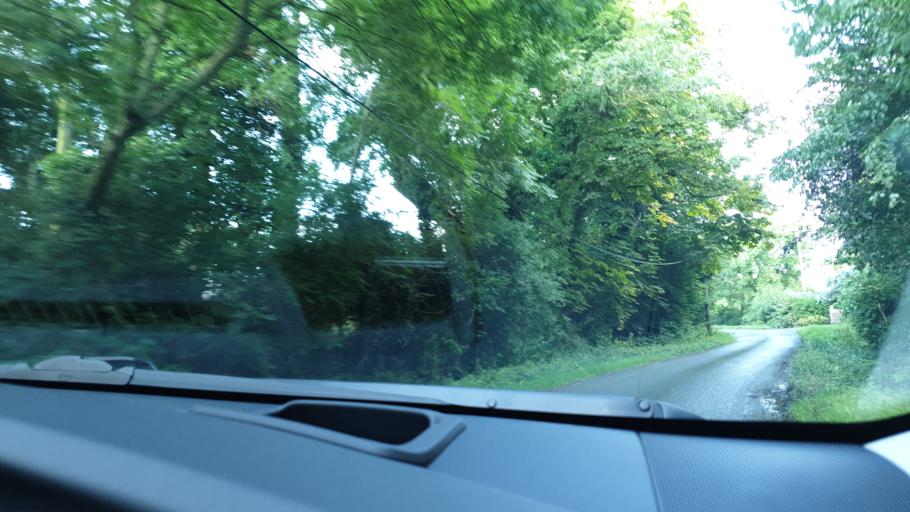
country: IE
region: Leinster
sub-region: An Mhi
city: Ashbourne
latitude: 53.4939
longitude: -6.4049
